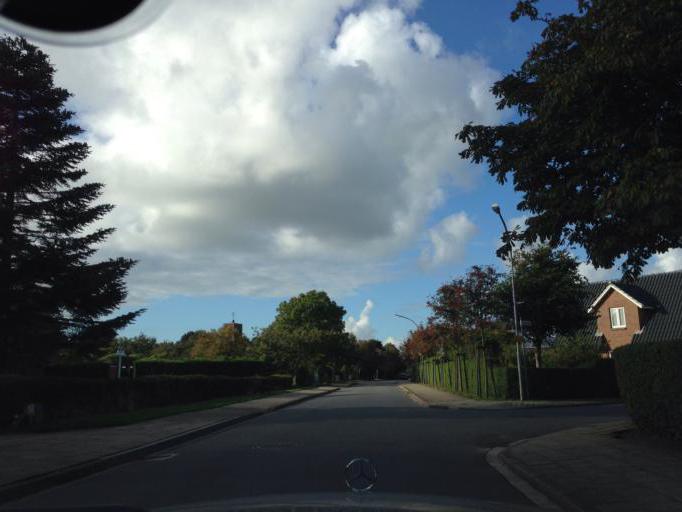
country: DE
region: Schleswig-Holstein
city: Wyk auf Fohr
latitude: 54.6895
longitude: 8.5601
